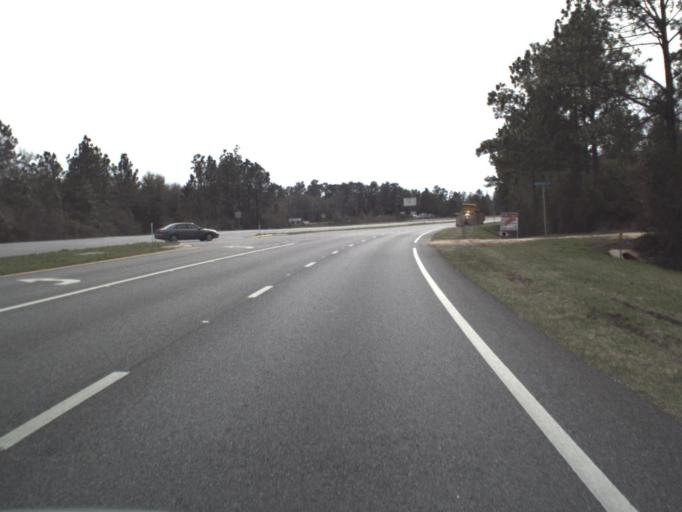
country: US
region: Florida
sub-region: Bay County
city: Youngstown
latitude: 30.5350
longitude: -85.3942
